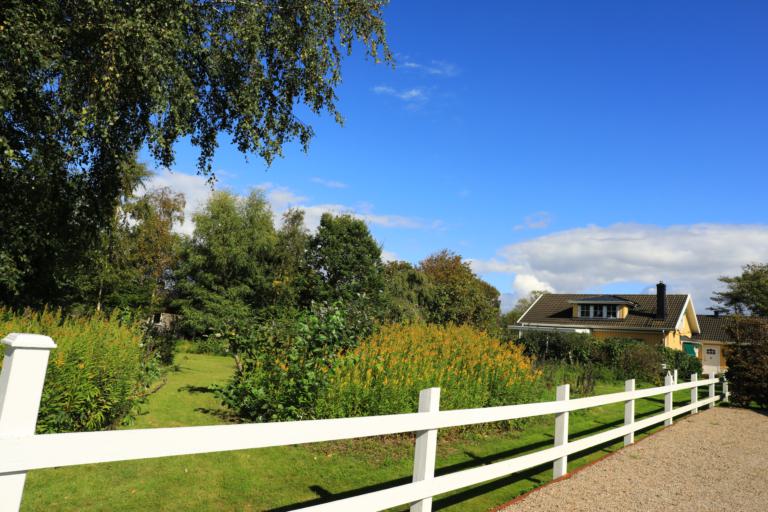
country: SE
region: Halland
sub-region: Varbergs Kommun
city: Traslovslage
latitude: 57.0765
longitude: 12.2671
